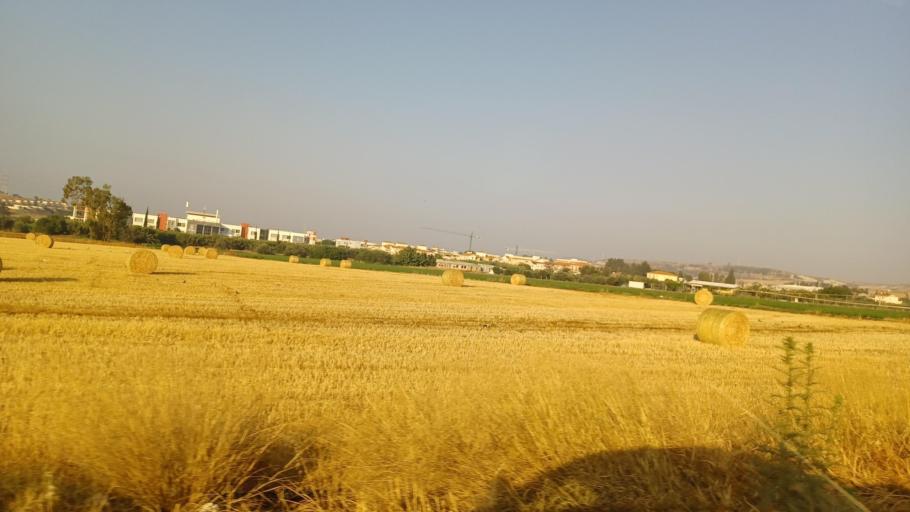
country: CY
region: Larnaka
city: Pyla
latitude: 35.0115
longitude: 33.6994
